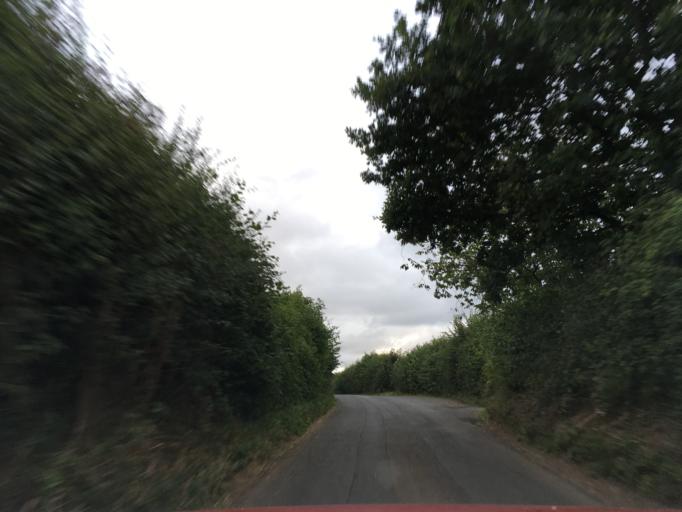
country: GB
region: England
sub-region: Wiltshire
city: Biddestone
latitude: 51.4500
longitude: -2.1988
